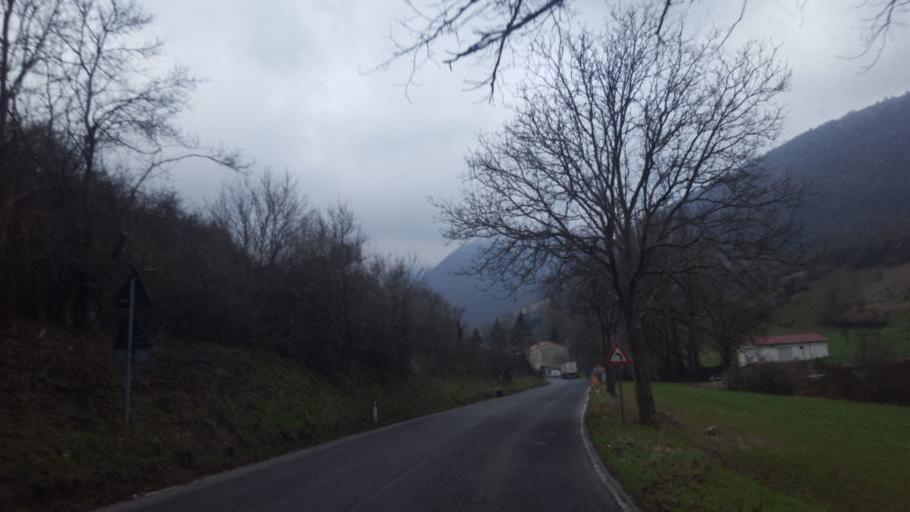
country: IT
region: The Marches
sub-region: Provincia di Macerata
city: Visso
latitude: 42.9480
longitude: 13.0840
